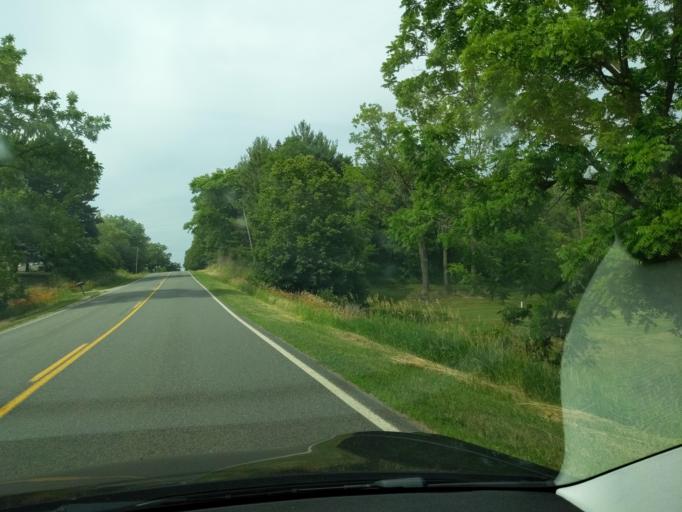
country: US
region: Michigan
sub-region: Clinton County
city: DeWitt
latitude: 42.8835
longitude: -84.6023
